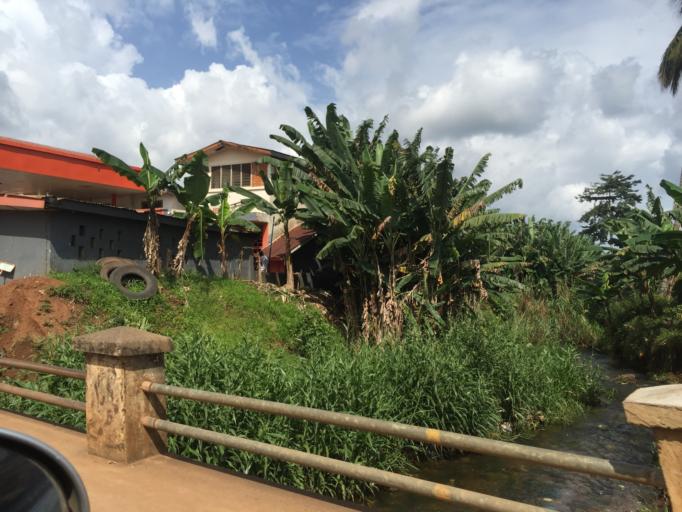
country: GH
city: Mpraeso
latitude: 6.5904
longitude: -0.7355
